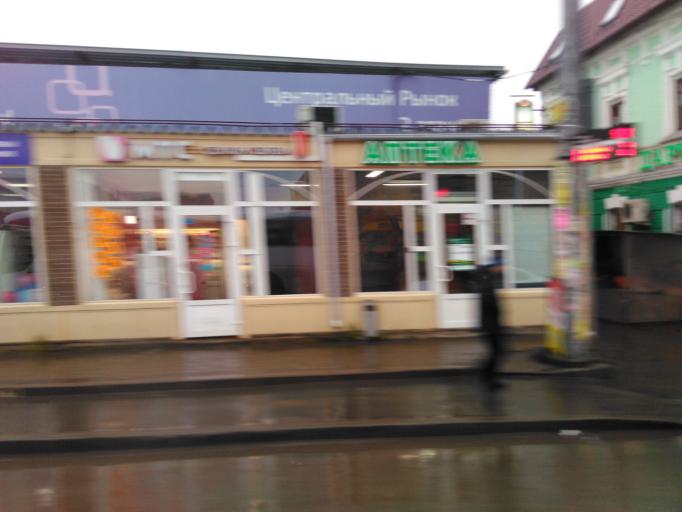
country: RU
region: Tatarstan
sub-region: Gorod Kazan'
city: Kazan
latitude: 55.7855
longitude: 49.1080
